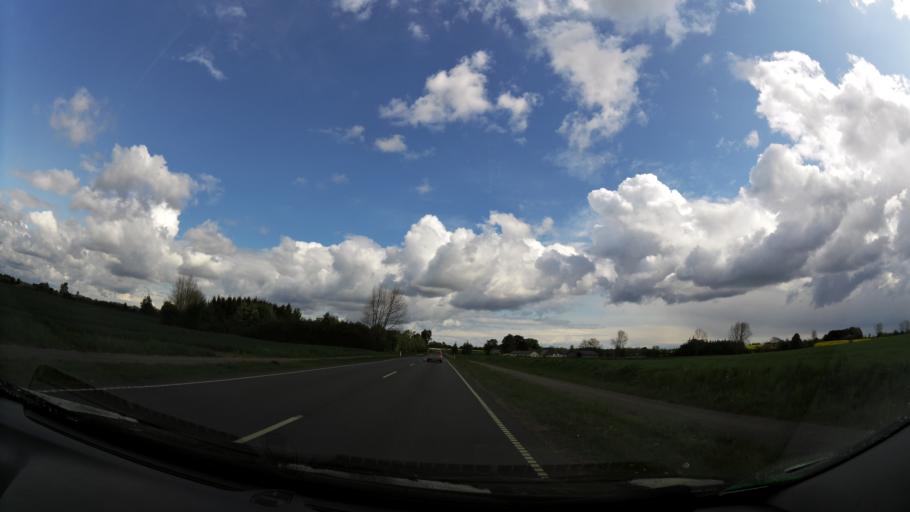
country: DK
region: South Denmark
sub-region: Svendborg Kommune
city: Thuro By
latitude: 55.1278
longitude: 10.7306
